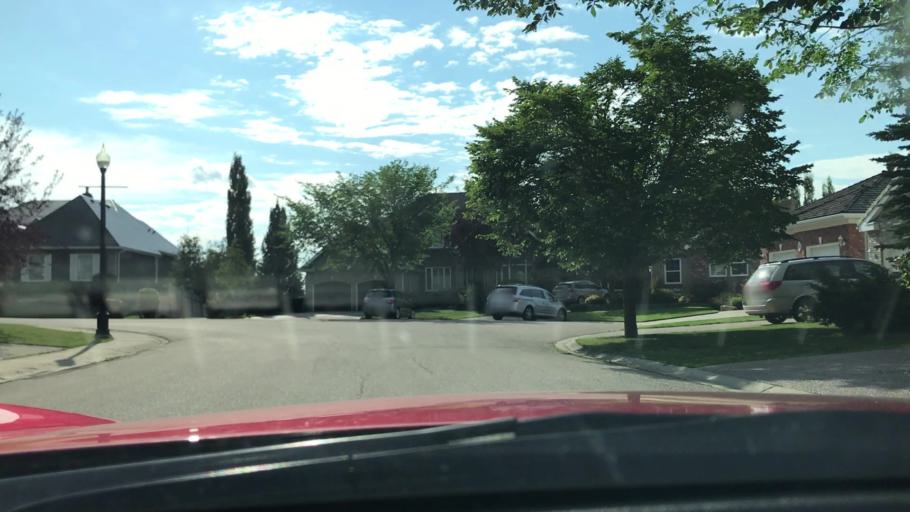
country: CA
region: Alberta
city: Calgary
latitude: 51.0265
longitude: -114.1753
